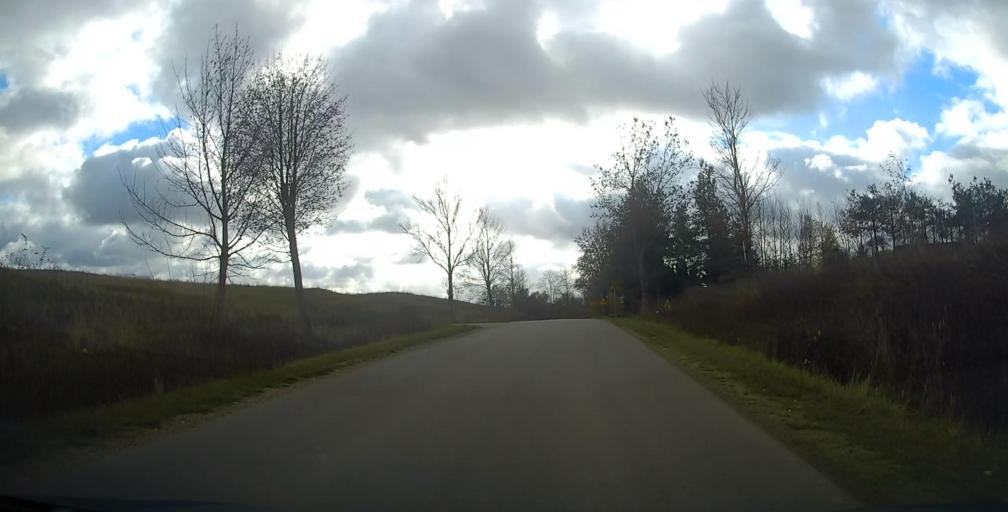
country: PL
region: Podlasie
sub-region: Suwalki
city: Suwalki
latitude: 54.3342
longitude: 22.8591
